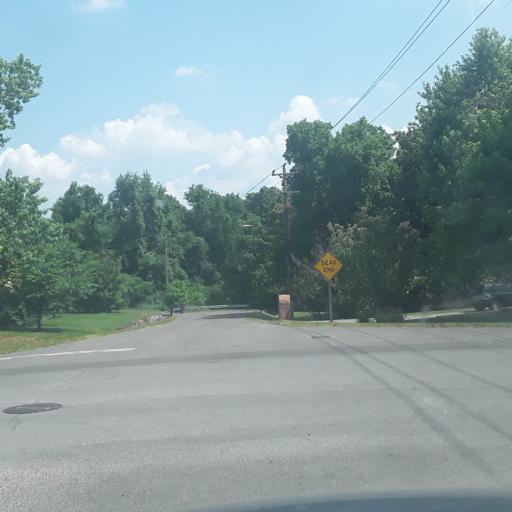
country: US
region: Tennessee
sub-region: Williamson County
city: Brentwood Estates
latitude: 36.0545
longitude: -86.7078
